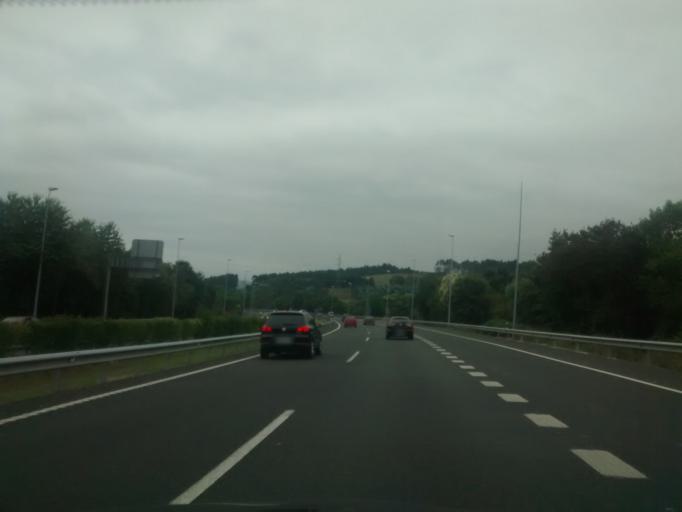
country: ES
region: Cantabria
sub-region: Provincia de Cantabria
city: Reocin
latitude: 43.3449
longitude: -4.1314
